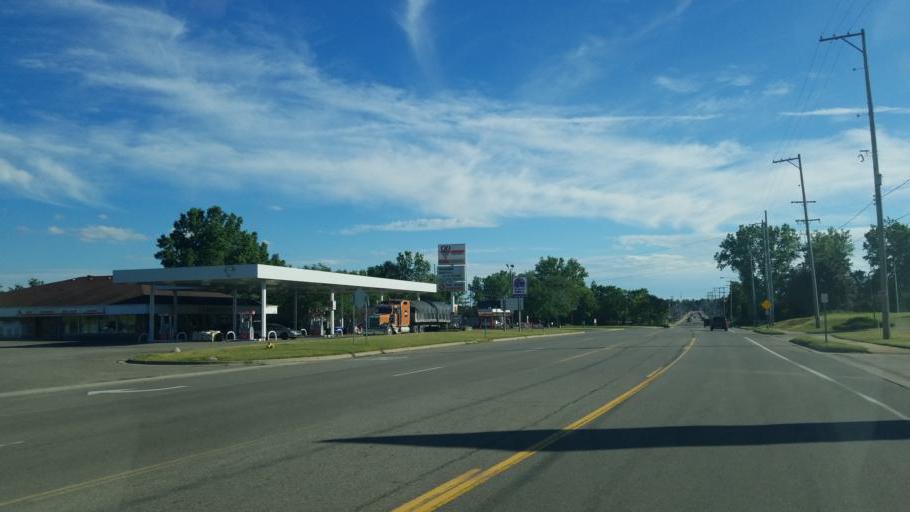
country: US
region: Michigan
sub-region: Eaton County
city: Charlotte
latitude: 42.5741
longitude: -84.8218
